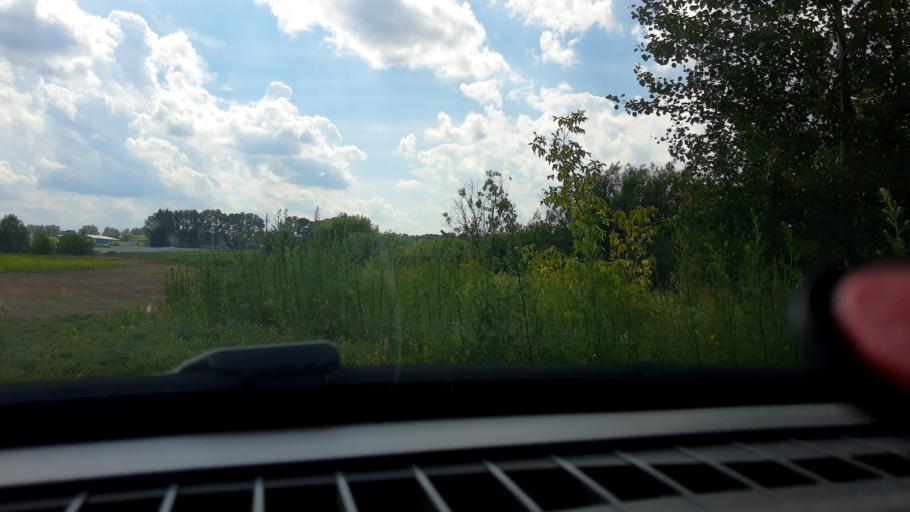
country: RU
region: Nizjnij Novgorod
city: Afonino
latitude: 56.2147
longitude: 44.1130
